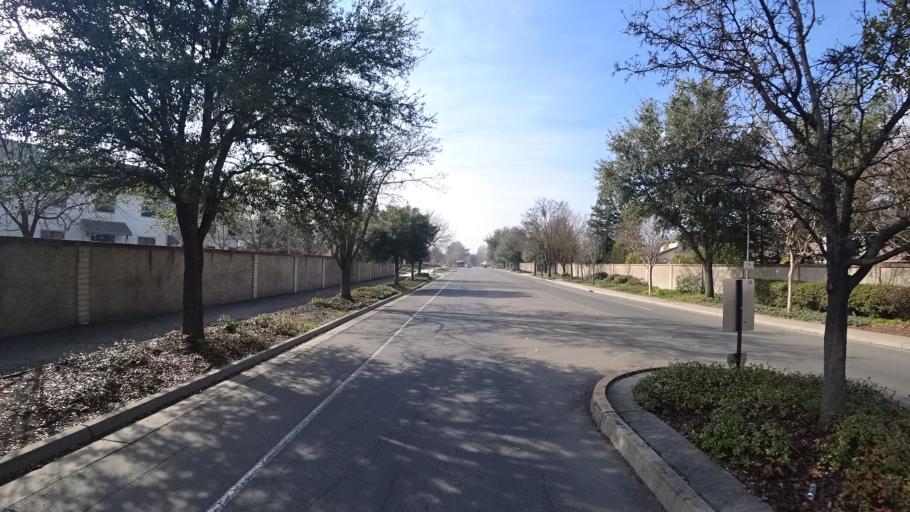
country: US
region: California
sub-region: Yolo County
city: Davis
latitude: 38.5523
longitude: -121.7171
